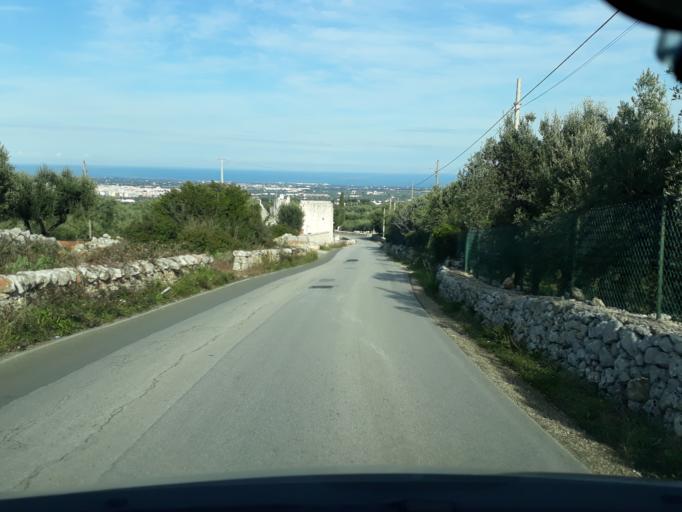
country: IT
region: Apulia
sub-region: Provincia di Brindisi
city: Lamie di Olimpie-Selva
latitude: 40.8076
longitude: 17.3533
